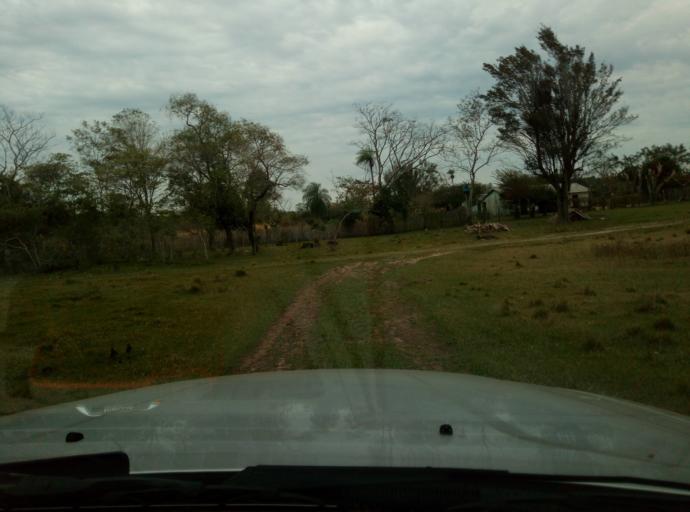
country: PY
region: Caaguazu
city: Carayao
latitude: -25.1609
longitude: -56.3340
